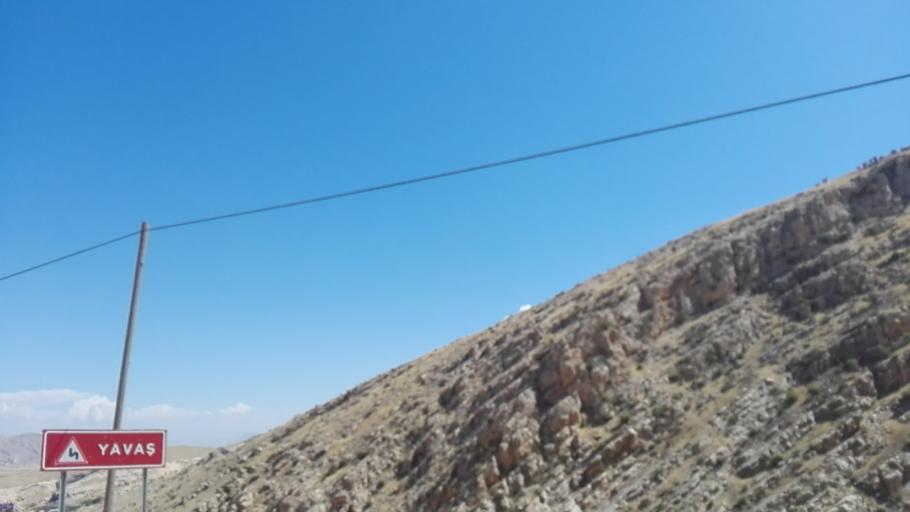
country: TR
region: Batman
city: Hasankeyf
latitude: 37.7009
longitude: 41.4607
